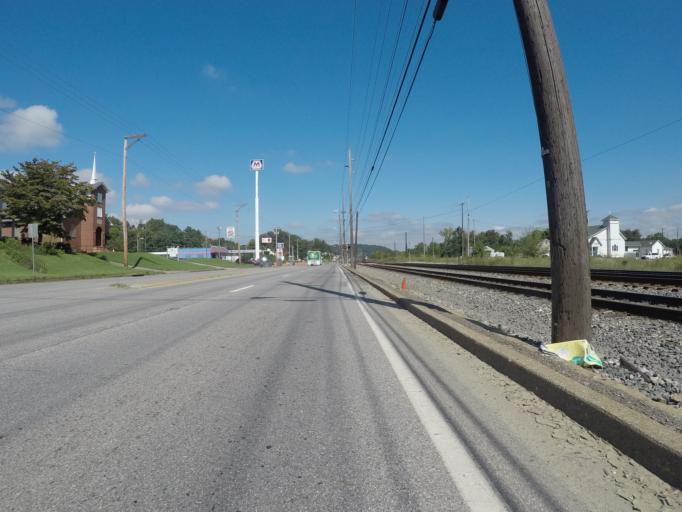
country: US
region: Ohio
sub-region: Lawrence County
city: South Point
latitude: 38.4375
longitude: -82.6080
